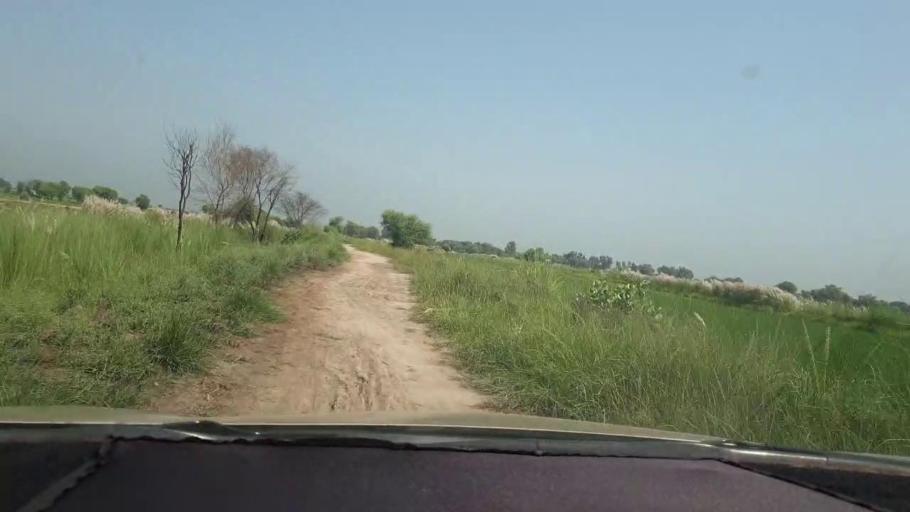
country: PK
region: Sindh
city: Kambar
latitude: 27.6042
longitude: 68.0641
